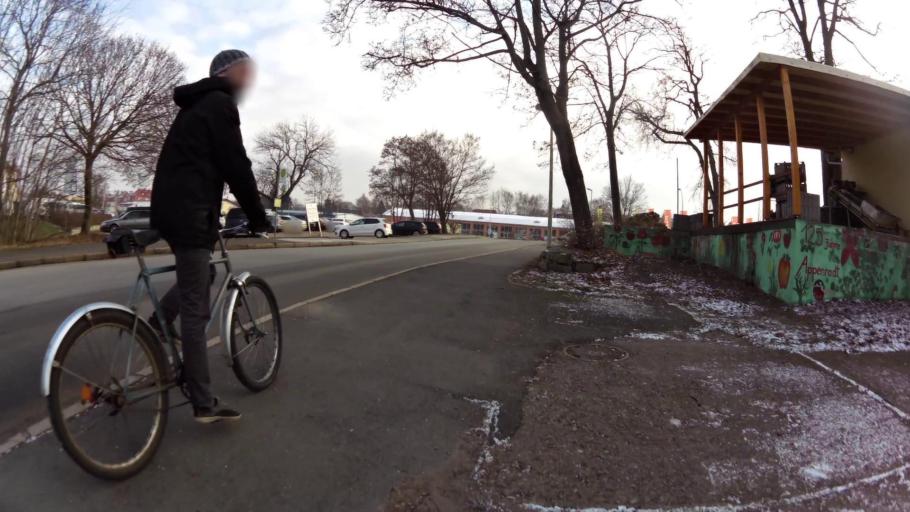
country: DE
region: Thuringia
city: Weimar
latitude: 50.9810
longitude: 11.3090
